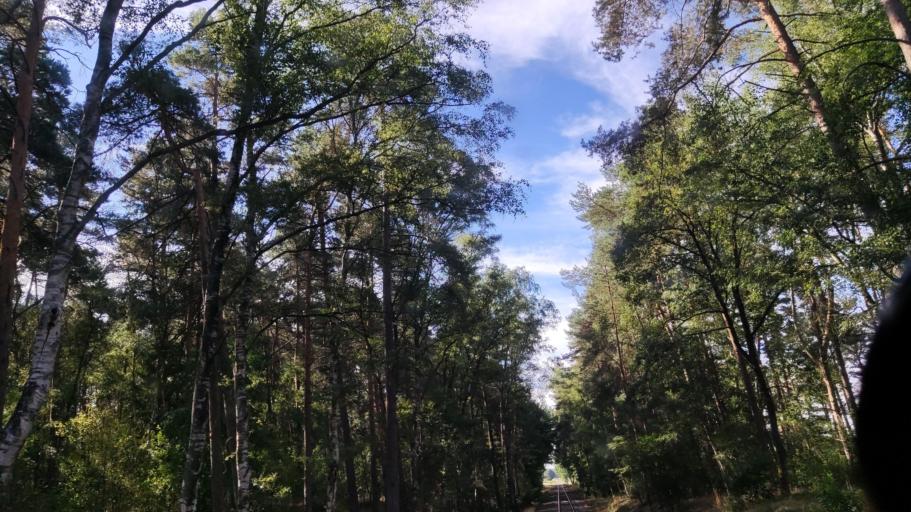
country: DE
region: Lower Saxony
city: Soltau
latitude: 53.0045
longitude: 9.8889
